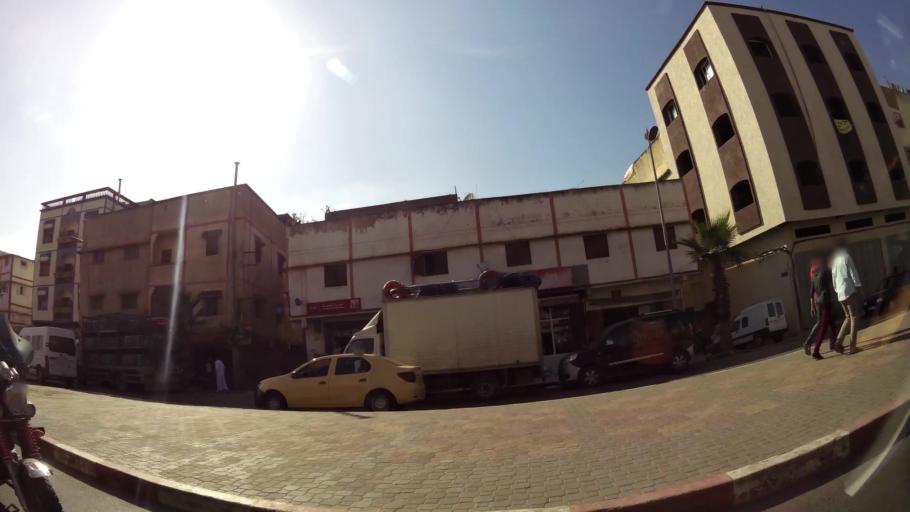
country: MA
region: Rabat-Sale-Zemmour-Zaer
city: Sale
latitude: 34.0593
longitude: -6.7760
